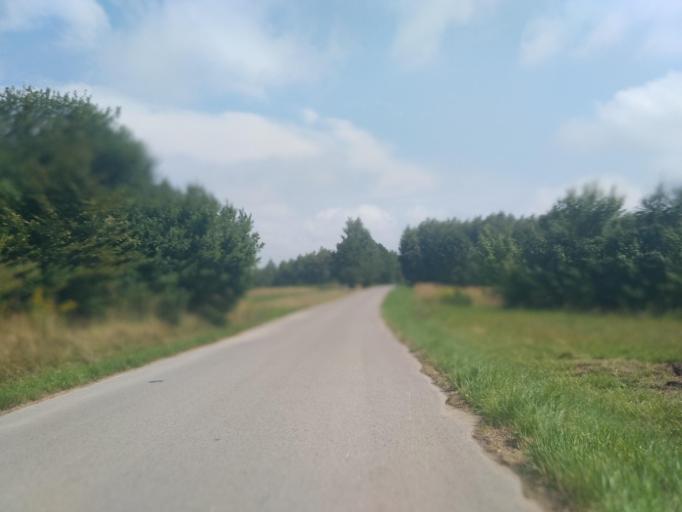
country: PL
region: Subcarpathian Voivodeship
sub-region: Powiat lancucki
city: Kraczkowa
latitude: 50.0206
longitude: 22.1400
